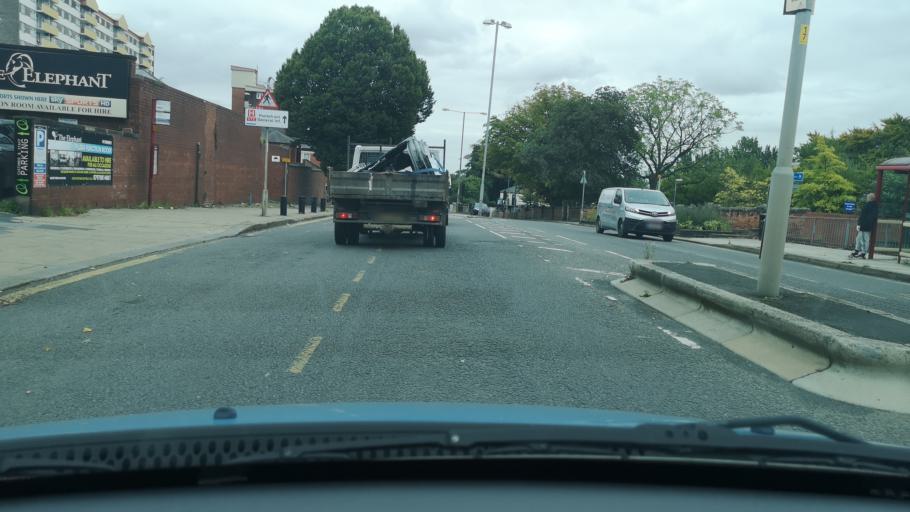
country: GB
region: England
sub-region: City and Borough of Wakefield
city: Pontefract
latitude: 53.6909
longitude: -1.3098
